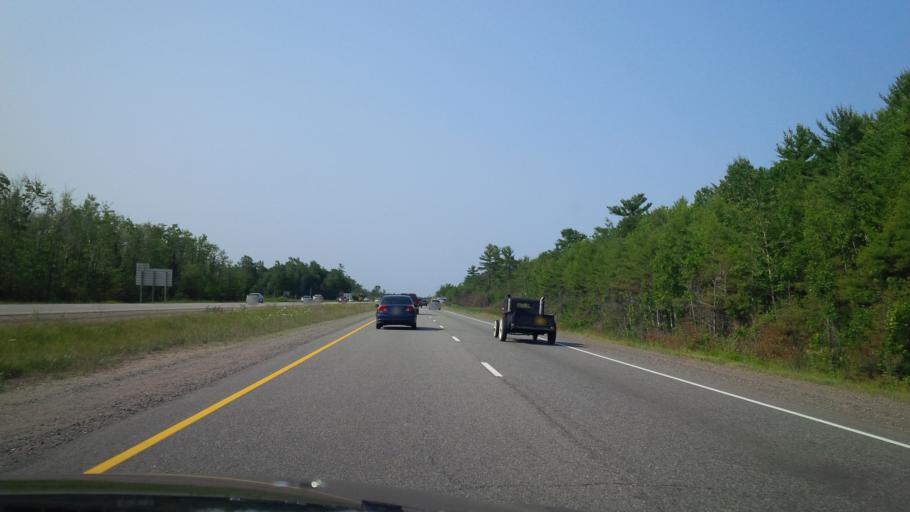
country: CA
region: Ontario
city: Bracebridge
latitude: 44.9696
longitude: -79.3211
